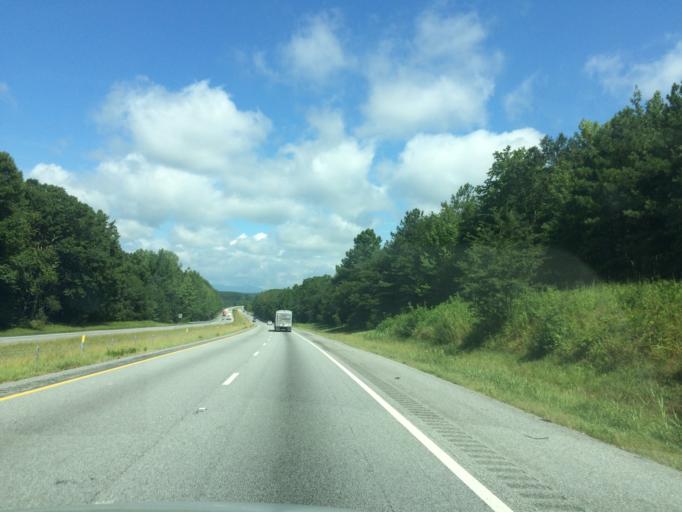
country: US
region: South Carolina
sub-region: Spartanburg County
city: Inman
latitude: 35.1009
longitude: -82.0763
